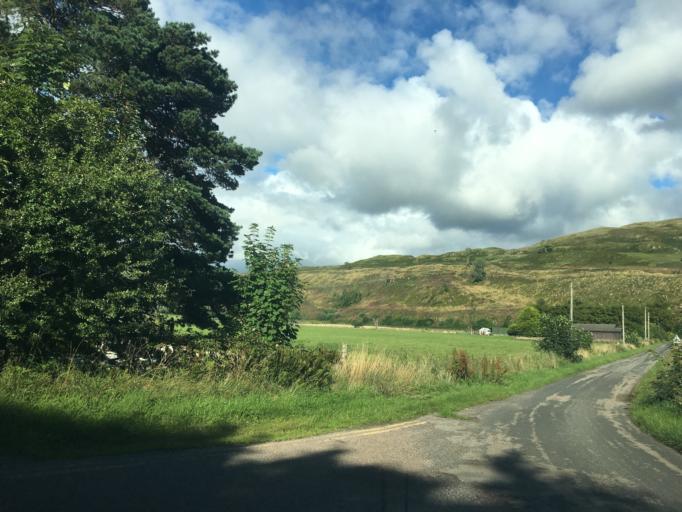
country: GB
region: Scotland
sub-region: Argyll and Bute
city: Lochgilphead
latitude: 56.1257
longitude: -5.4943
